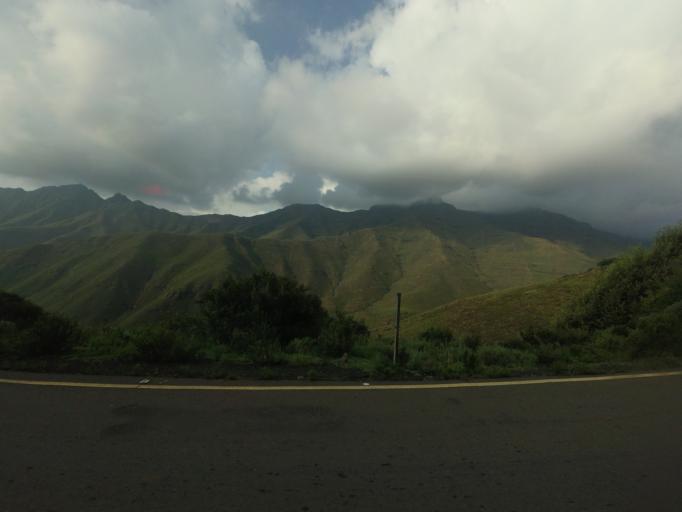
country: LS
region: Butha-Buthe
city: Butha-Buthe
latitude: -29.0617
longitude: 28.3623
